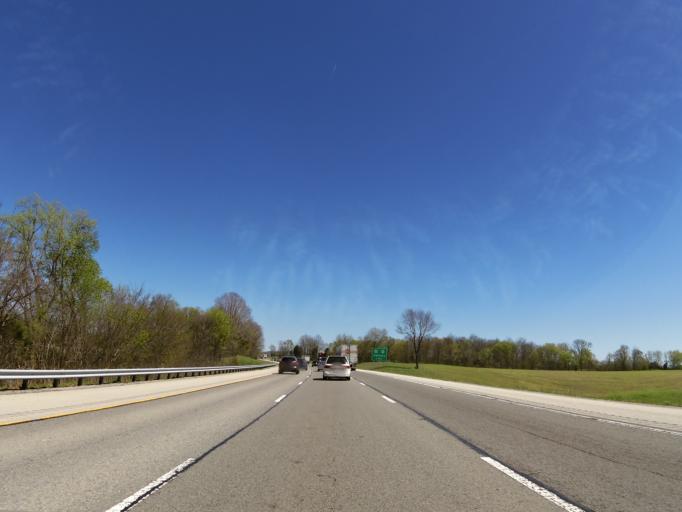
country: US
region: Kentucky
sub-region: Edmonson County
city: Brownsville
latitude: 37.0192
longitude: -86.2577
